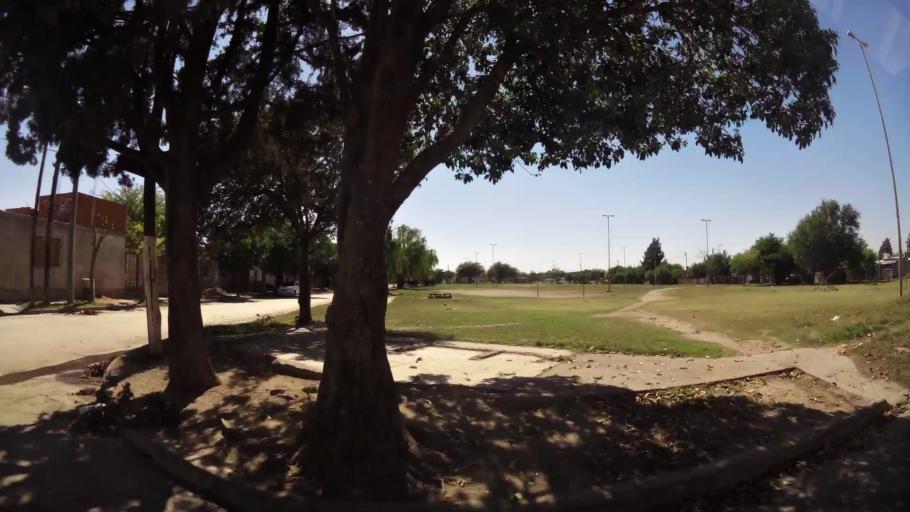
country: AR
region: Cordoba
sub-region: Departamento de Capital
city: Cordoba
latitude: -31.4419
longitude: -64.1305
